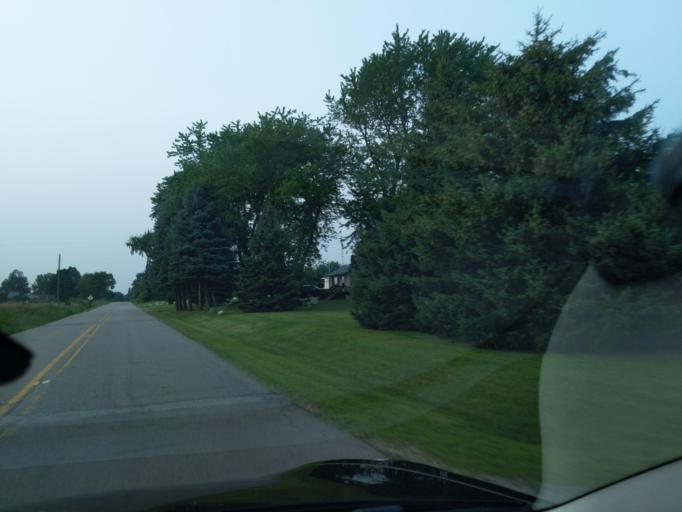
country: US
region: Michigan
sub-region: Jackson County
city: Jackson
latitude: 42.3283
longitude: -84.4334
